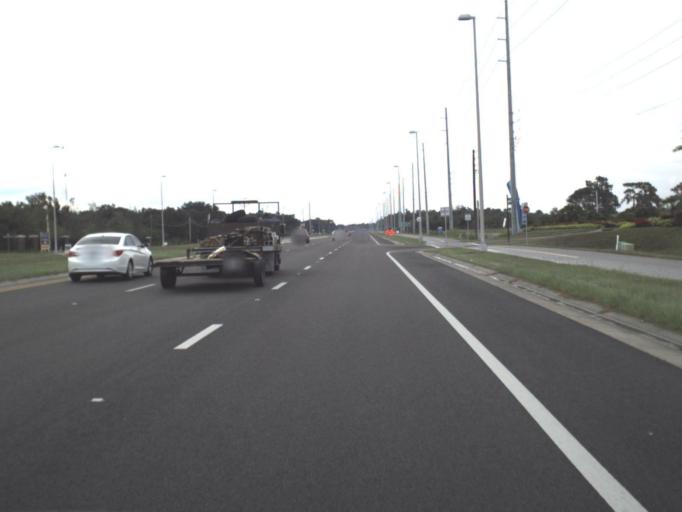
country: US
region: Florida
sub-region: Hillsborough County
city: Riverview
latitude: 27.8282
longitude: -82.3297
